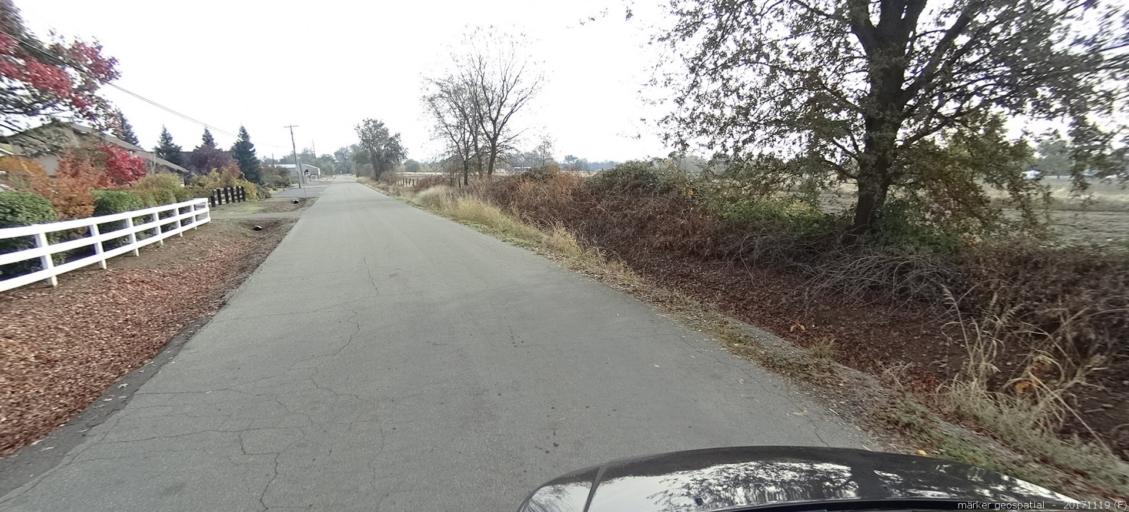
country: US
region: California
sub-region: Shasta County
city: Redding
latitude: 40.5222
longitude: -122.3393
